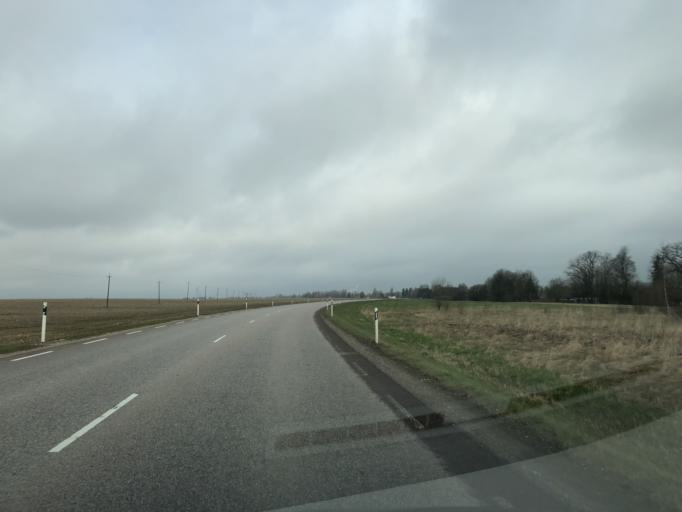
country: EE
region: Jogevamaa
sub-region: Jogeva linn
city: Jogeva
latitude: 58.7159
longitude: 26.3984
